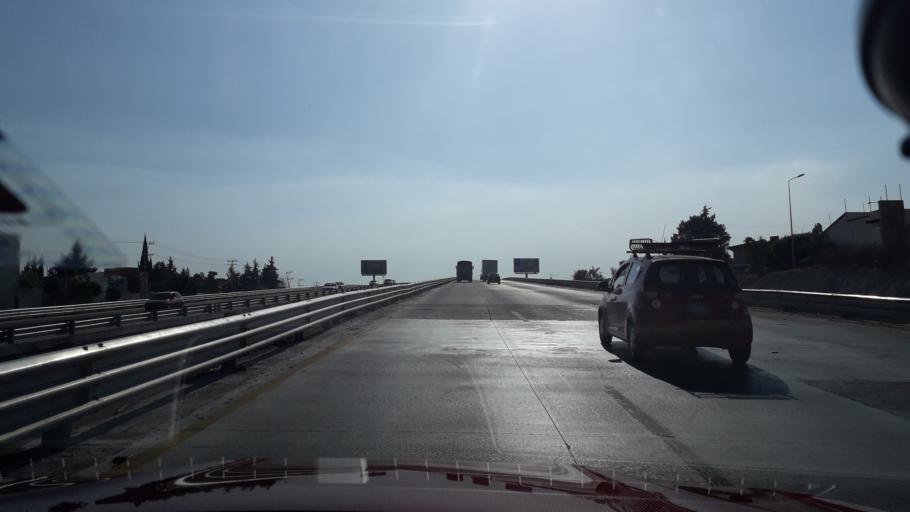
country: MX
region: Puebla
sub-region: Puebla
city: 18 de Marzo
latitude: 18.9719
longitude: -98.1951
